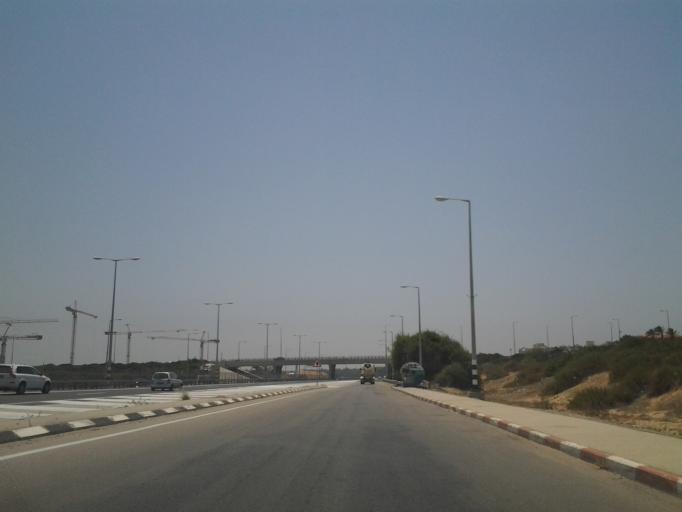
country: IL
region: Haifa
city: Hadera
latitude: 32.4461
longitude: 34.8926
